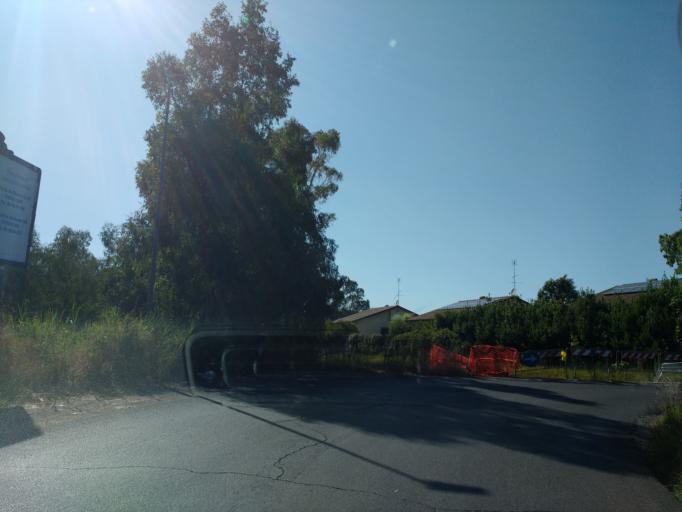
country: IT
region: Latium
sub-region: Citta metropolitana di Roma Capitale
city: Acilia-Castel Fusano-Ostia Antica
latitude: 41.7495
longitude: 12.3306
